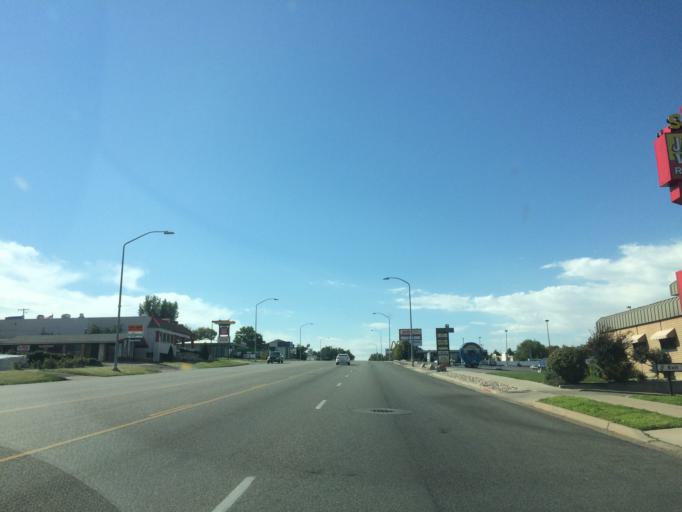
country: US
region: Utah
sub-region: Weber County
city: South Ogden
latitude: 41.1951
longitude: -111.9712
